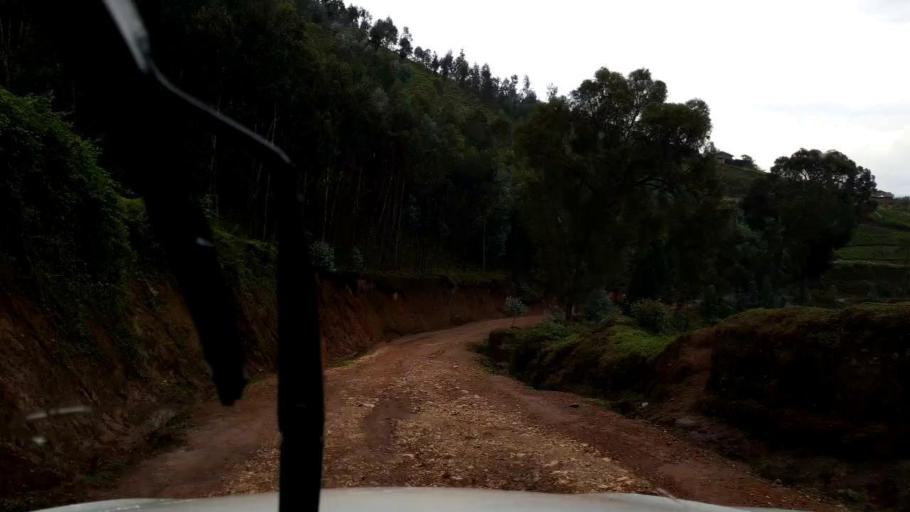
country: RW
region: Western Province
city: Kibuye
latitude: -2.0193
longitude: 29.4620
